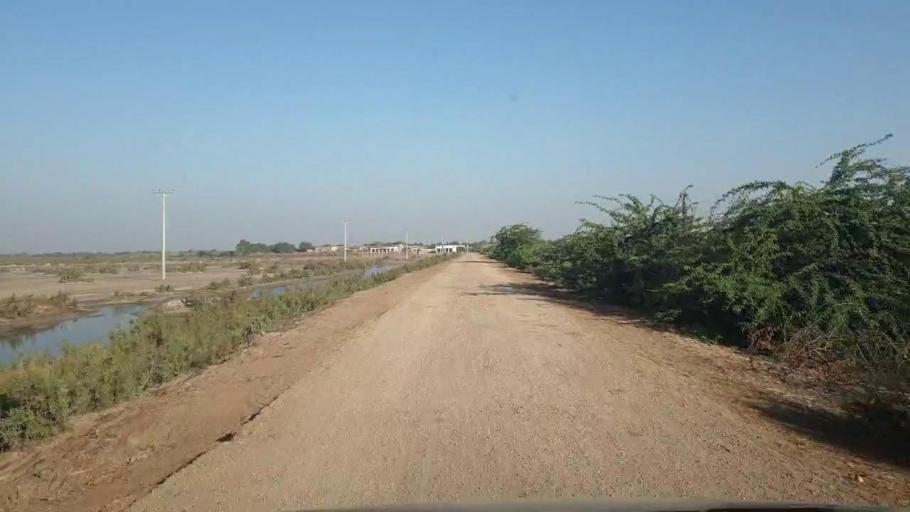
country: PK
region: Sindh
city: Badin
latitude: 24.6985
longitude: 68.8163
